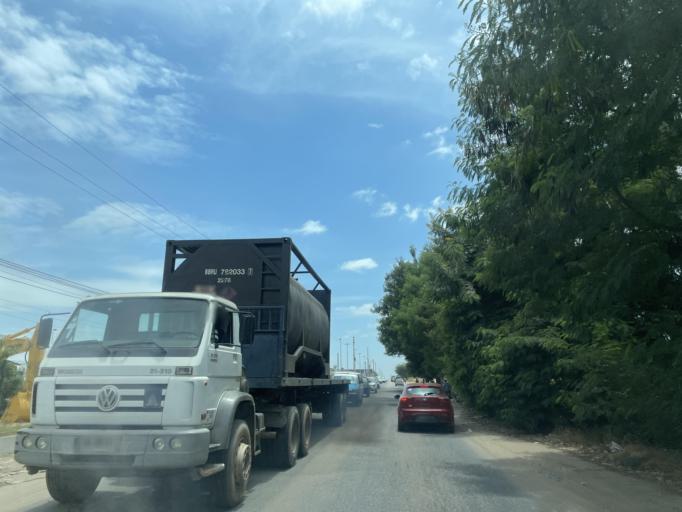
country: AO
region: Luanda
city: Luanda
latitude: -8.9360
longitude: 13.3906
